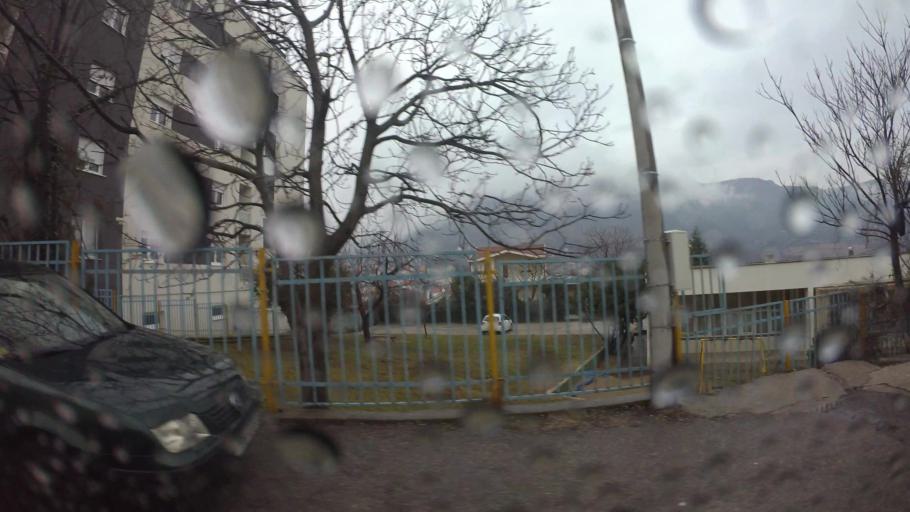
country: BA
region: Federation of Bosnia and Herzegovina
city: Cim
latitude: 43.3476
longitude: 17.7925
